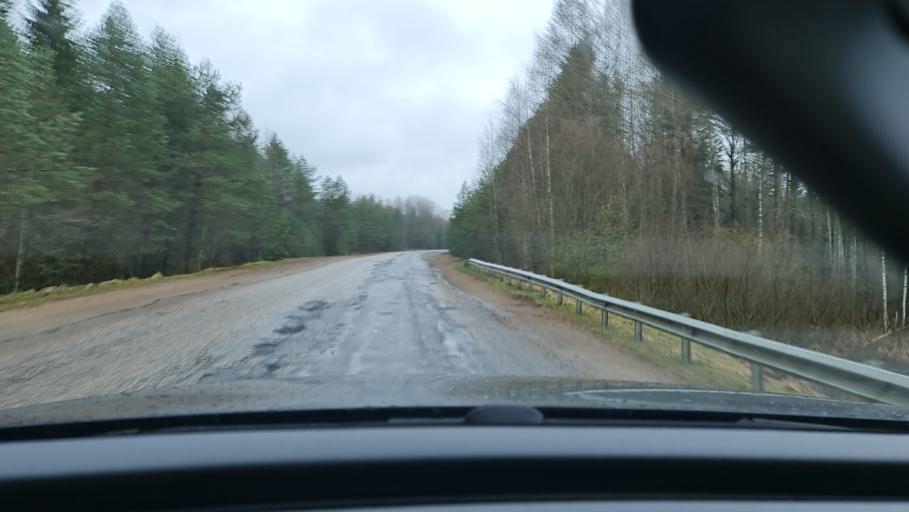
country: RU
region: Novgorod
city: Valday
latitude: 58.0378
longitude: 32.8977
